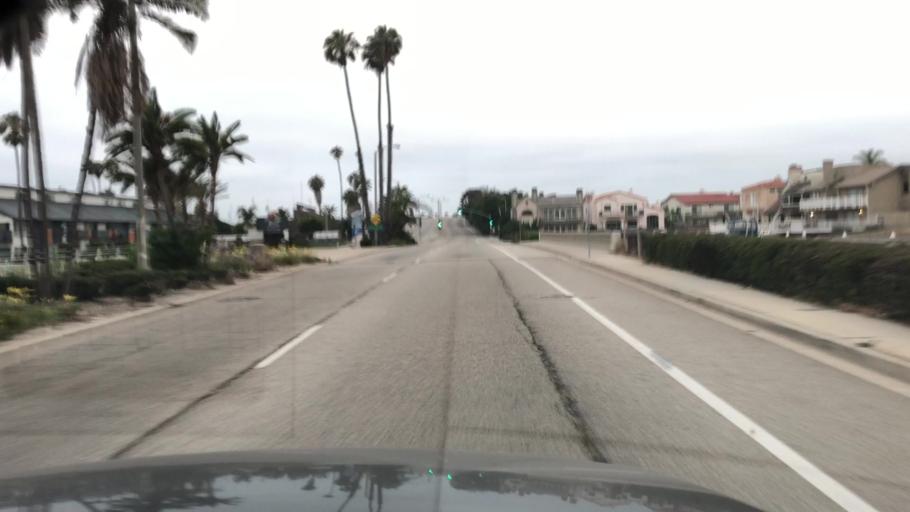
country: US
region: California
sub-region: Ventura County
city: Channel Islands Beach
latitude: 34.1758
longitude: -119.2232
